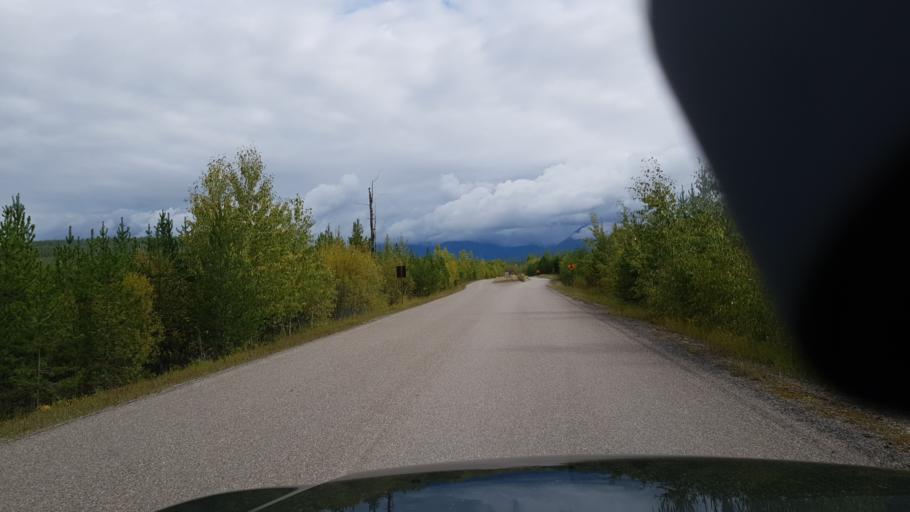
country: US
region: Montana
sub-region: Flathead County
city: Columbia Falls
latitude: 48.6260
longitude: -114.1287
